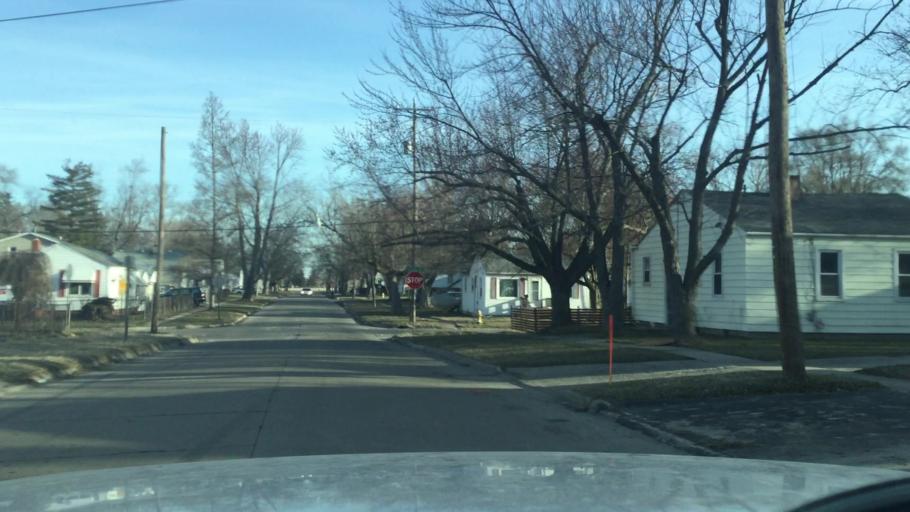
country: US
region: Michigan
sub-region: Genesee County
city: Flint
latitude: 42.9886
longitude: -83.6988
